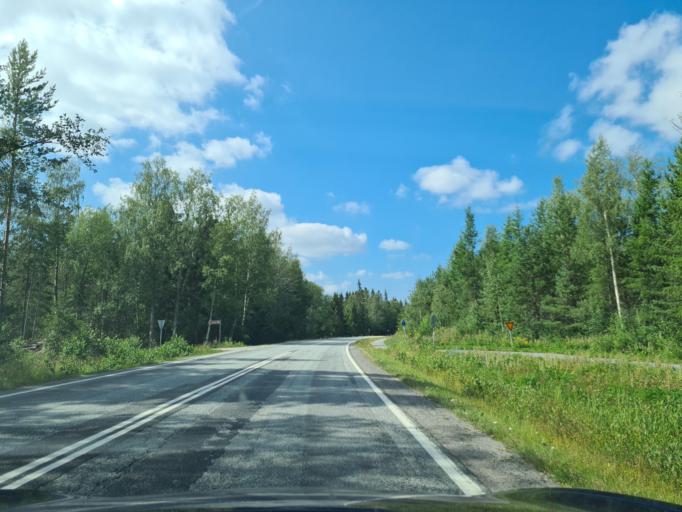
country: FI
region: Ostrobothnia
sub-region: Vaasa
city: Vaasa
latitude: 63.1951
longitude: 21.5495
